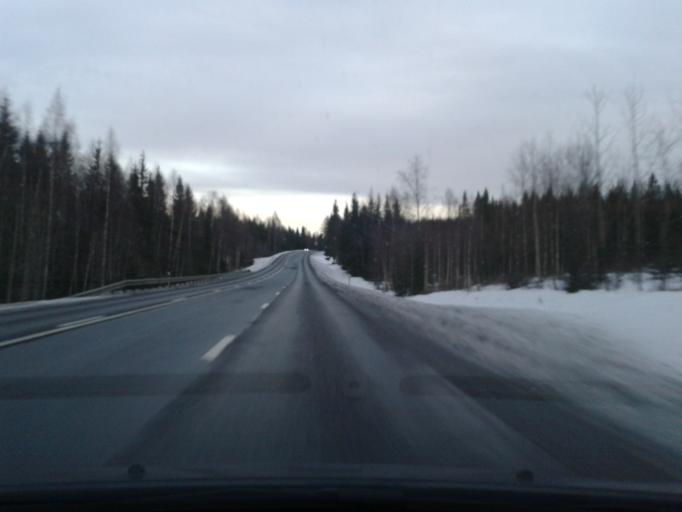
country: SE
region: Vaesternorrland
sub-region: Solleftea Kommun
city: Solleftea
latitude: 63.1378
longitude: 17.4418
